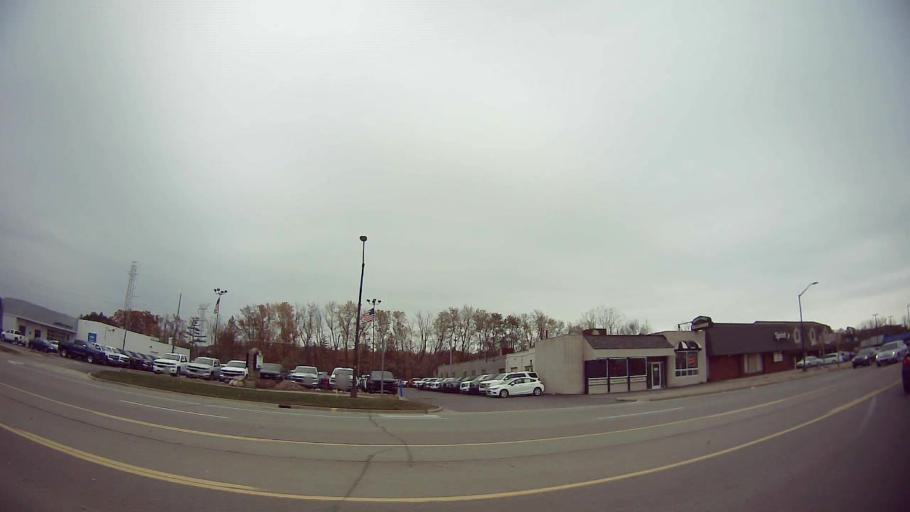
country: US
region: Michigan
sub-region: Oakland County
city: Clarkston
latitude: 42.7197
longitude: -83.4177
